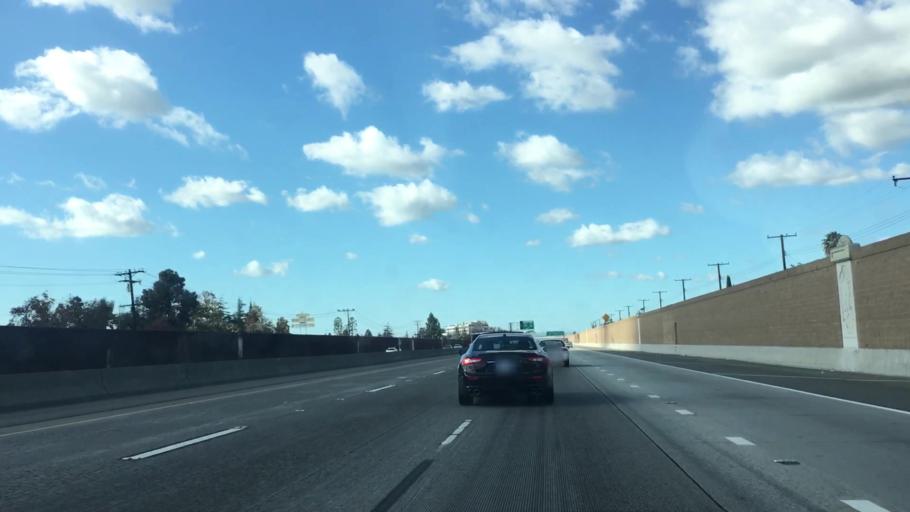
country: US
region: California
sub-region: Orange County
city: Westminster
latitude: 33.7744
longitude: -118.0241
